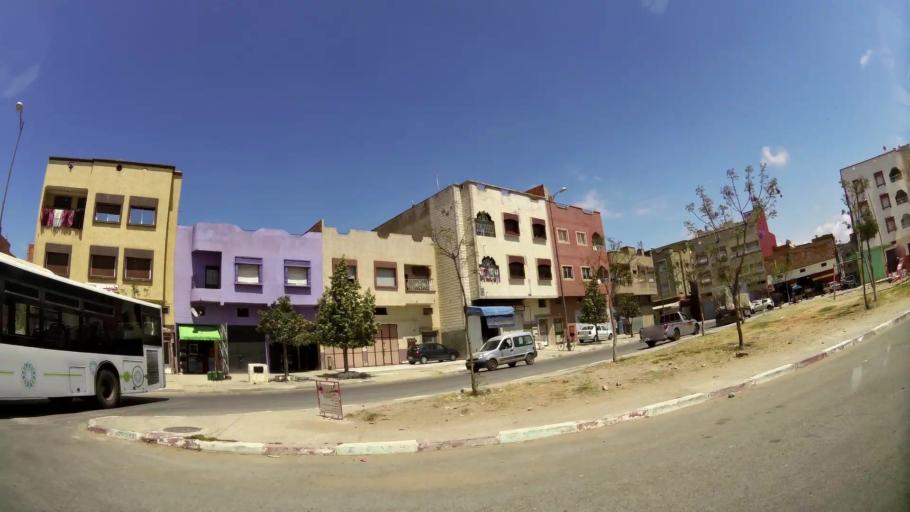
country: MA
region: Gharb-Chrarda-Beni Hssen
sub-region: Kenitra Province
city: Kenitra
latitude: 34.2504
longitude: -6.5405
